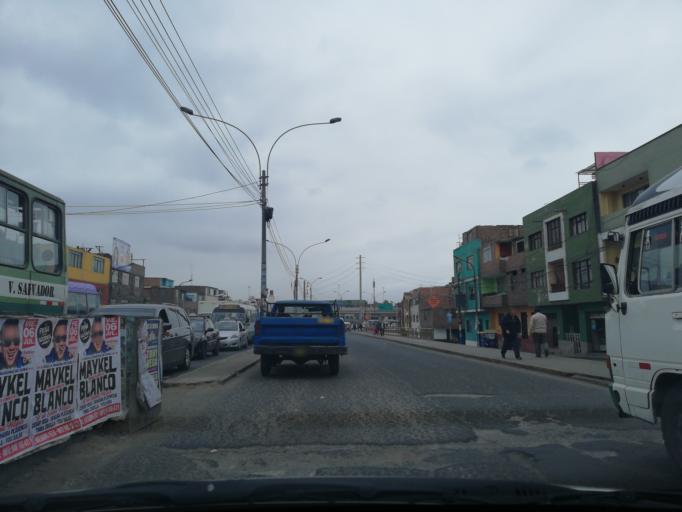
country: PE
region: Lima
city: Lima
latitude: -12.0332
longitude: -77.0651
